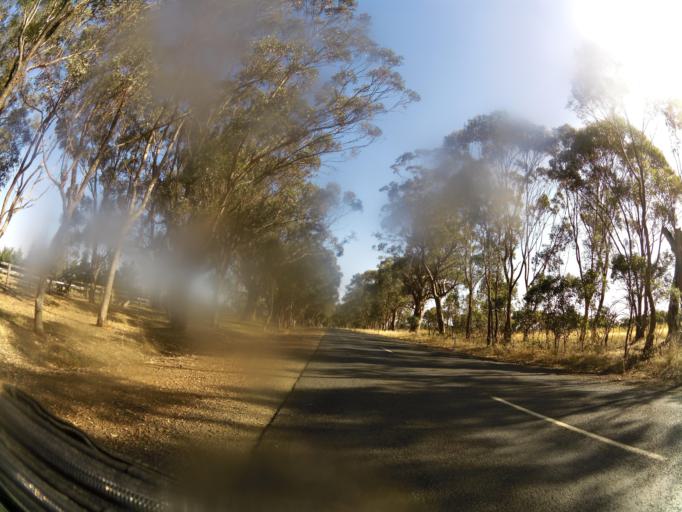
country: AU
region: Victoria
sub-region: Murrindindi
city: Kinglake West
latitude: -36.9706
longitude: 145.1093
